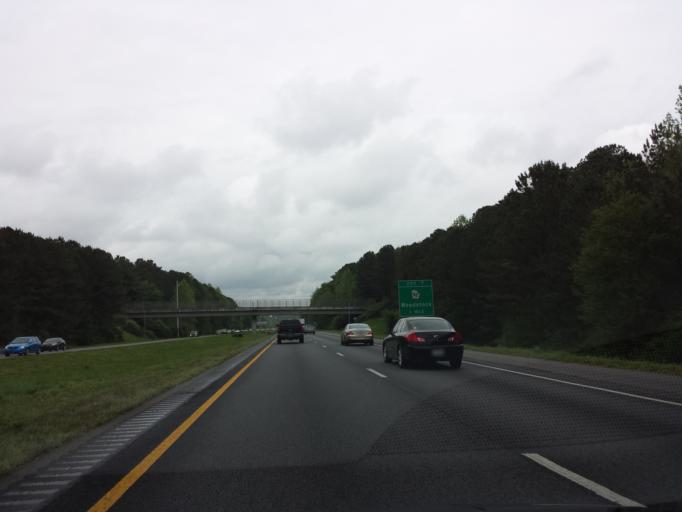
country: US
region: Georgia
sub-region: Cherokee County
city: Woodstock
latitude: 34.0666
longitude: -84.5405
